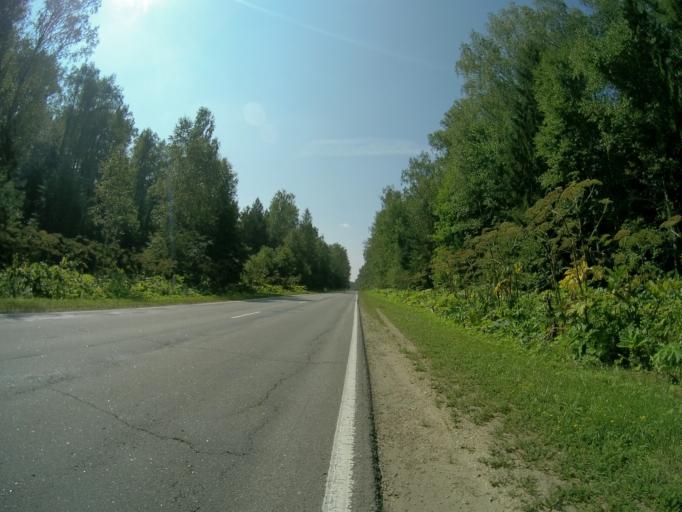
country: RU
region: Vladimir
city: Anopino
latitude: 55.7708
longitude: 40.6736
